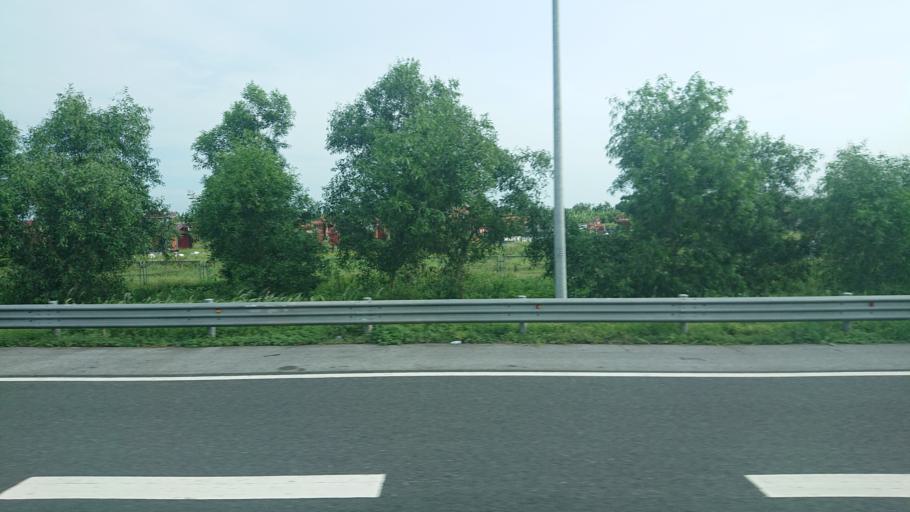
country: VN
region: Hai Phong
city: An Lao
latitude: 20.8017
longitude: 106.5292
